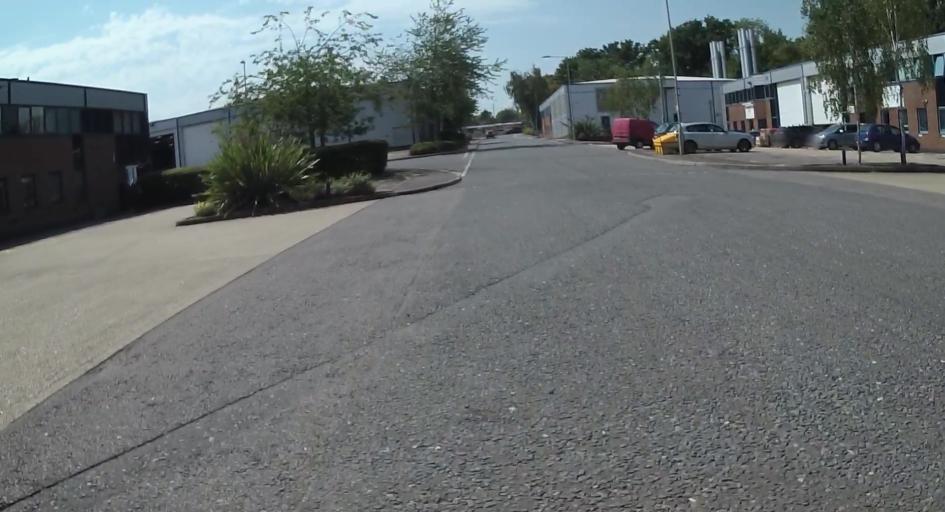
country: GB
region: England
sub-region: Hampshire
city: Basingstoke
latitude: 51.2784
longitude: -1.0636
